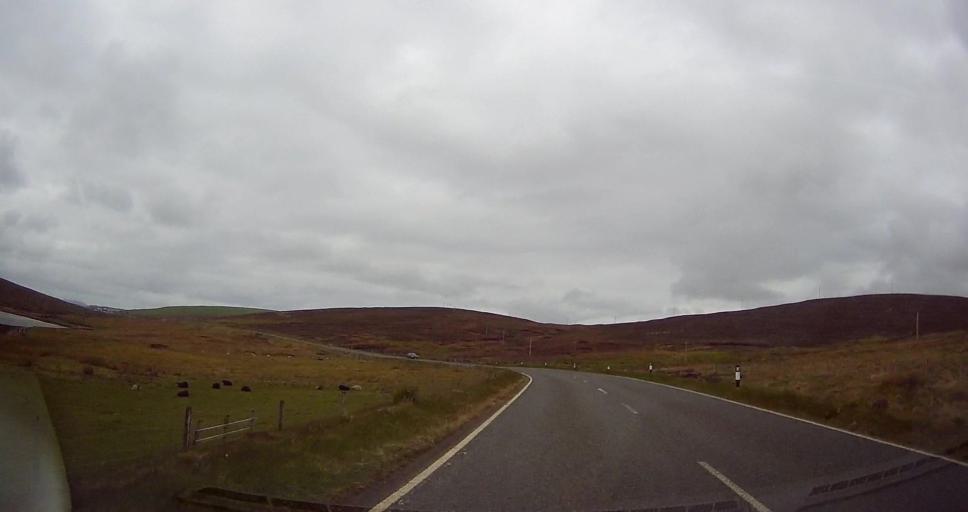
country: GB
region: Scotland
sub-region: Shetland Islands
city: Lerwick
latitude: 60.2481
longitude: -1.3710
